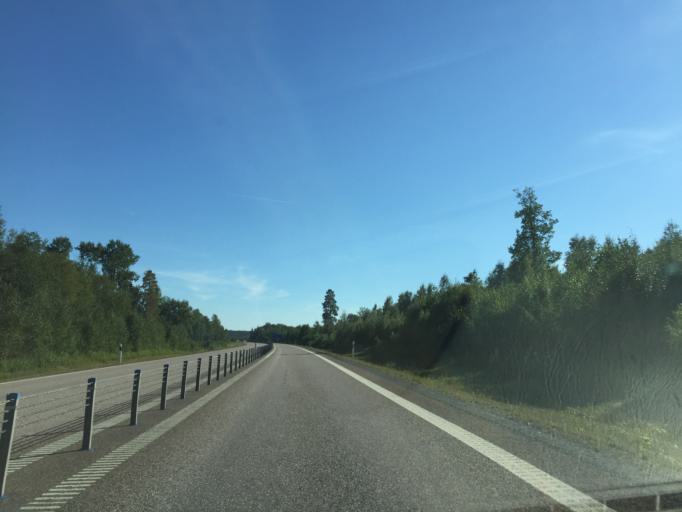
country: SE
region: Vaestmanland
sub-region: Arboga Kommun
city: Arboga
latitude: 59.4156
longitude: 15.8850
